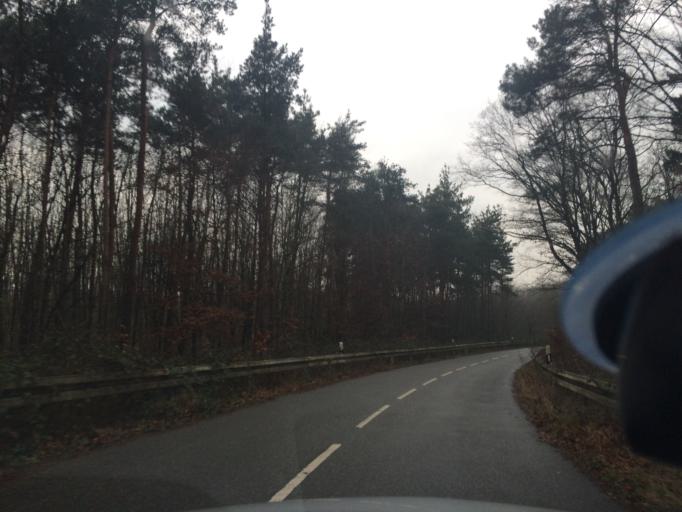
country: DE
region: Hesse
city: Morfelden-Walldorf
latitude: 50.0348
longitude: 8.6003
